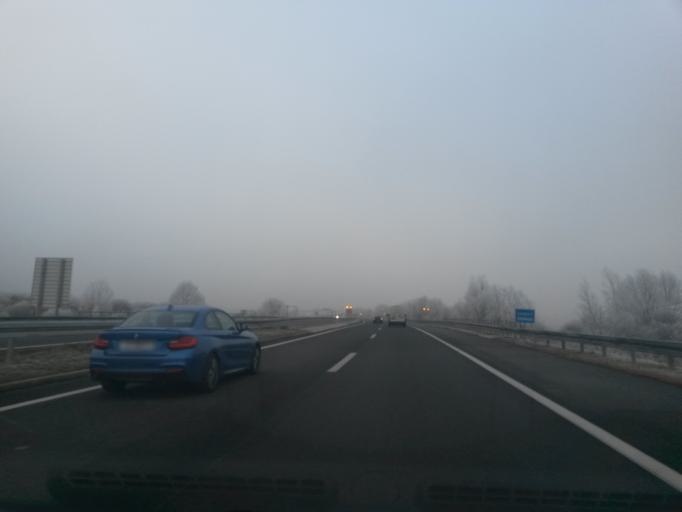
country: HR
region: Zagrebacka
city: Brckovljani
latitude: 45.9134
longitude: 16.2753
